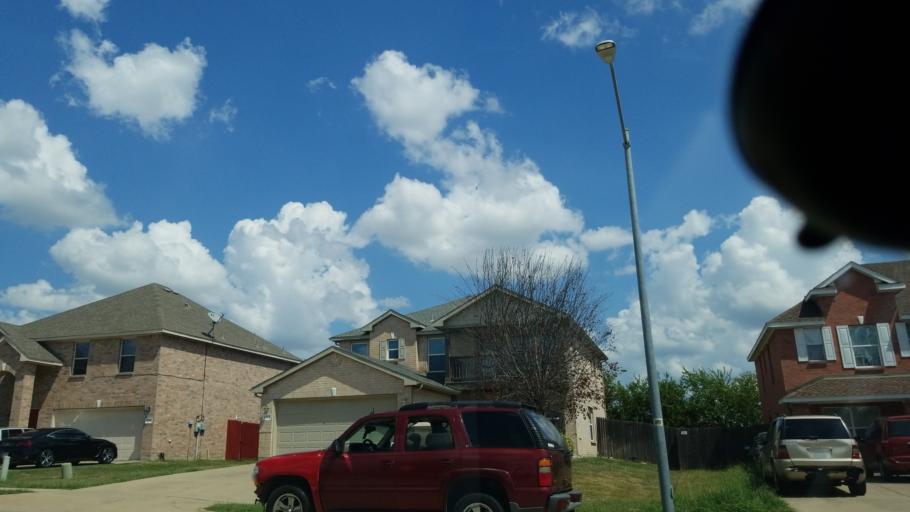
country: US
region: Texas
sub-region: Dallas County
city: Grand Prairie
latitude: 32.7283
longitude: -96.9964
